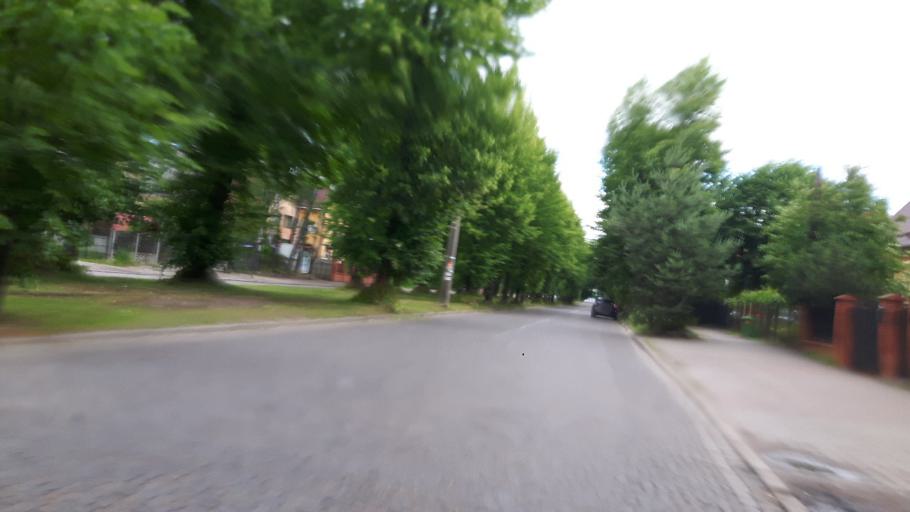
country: RU
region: Kaliningrad
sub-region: Gorod Kaliningrad
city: Kaliningrad
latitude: 54.7393
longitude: 20.5278
